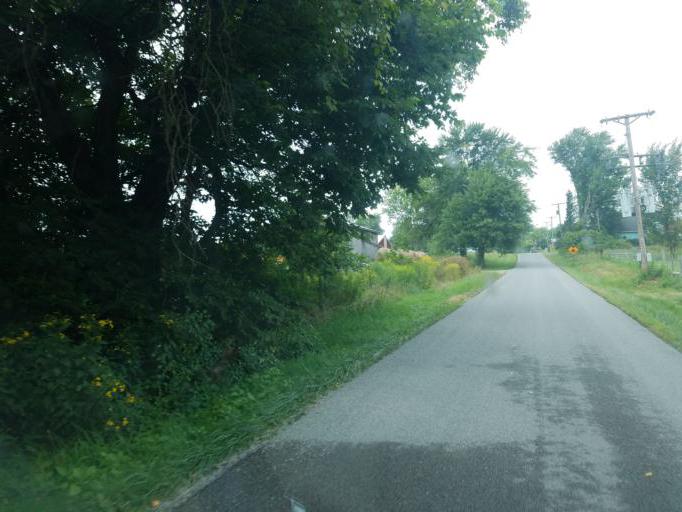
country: US
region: Ohio
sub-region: Morrow County
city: Cardington
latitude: 40.4188
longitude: -82.8532
